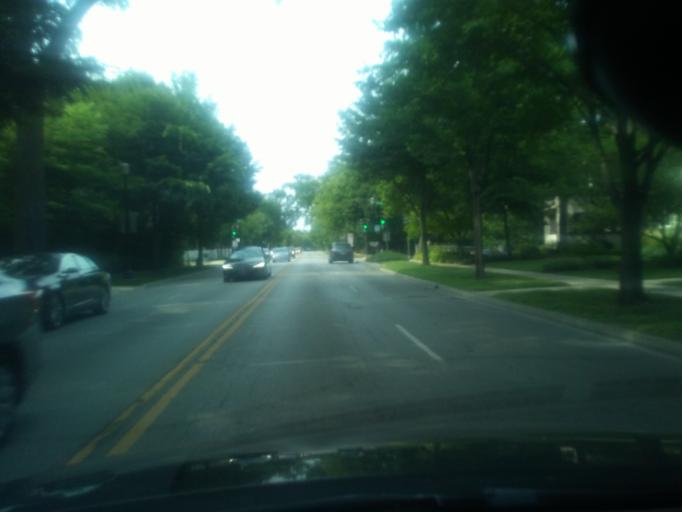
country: US
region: Illinois
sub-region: Cook County
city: Evanston
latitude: 42.0371
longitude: -87.6875
